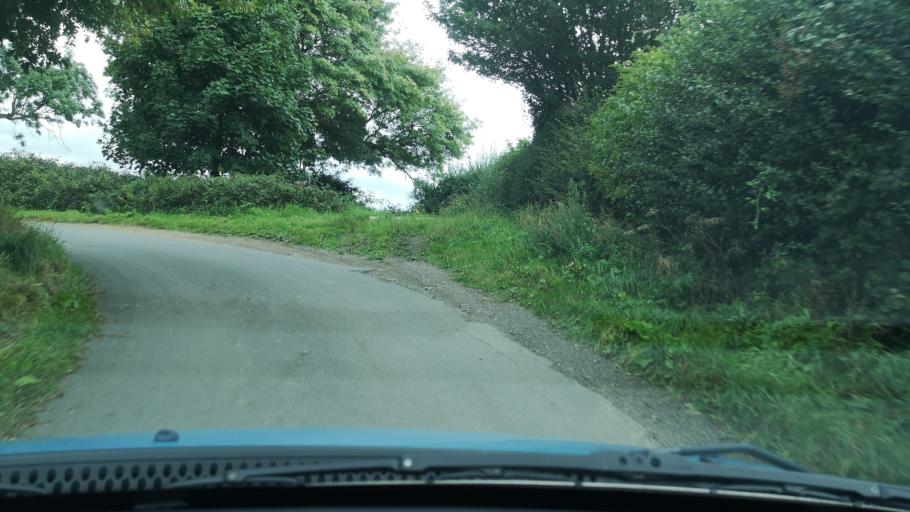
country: GB
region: England
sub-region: City and Borough of Wakefield
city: Fitzwilliam
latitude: 53.6466
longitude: -1.3600
